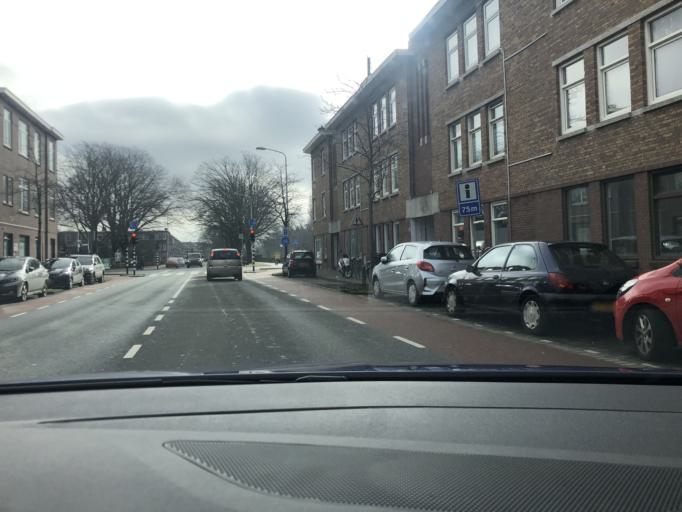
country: NL
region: South Holland
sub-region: Gemeente Den Haag
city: The Hague
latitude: 52.0712
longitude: 4.2675
